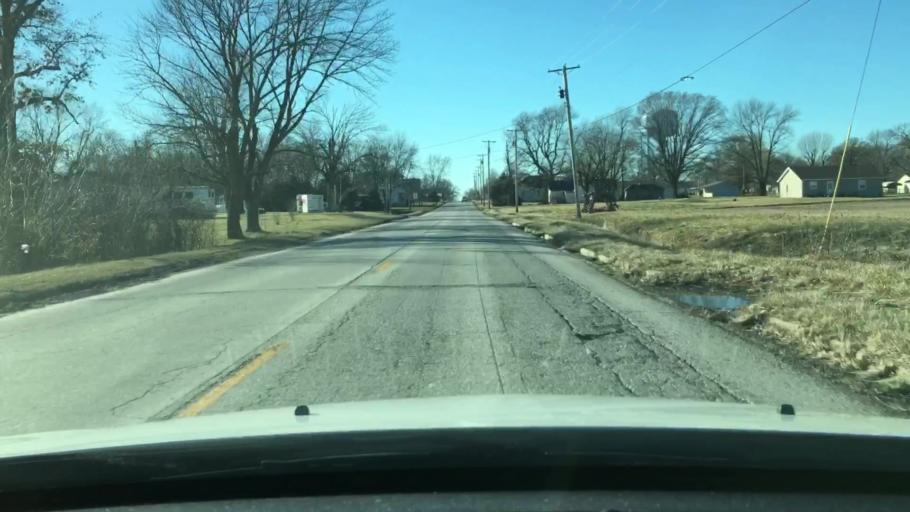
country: US
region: Missouri
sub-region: Pike County
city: Bowling Green
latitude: 39.3453
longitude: -91.3359
